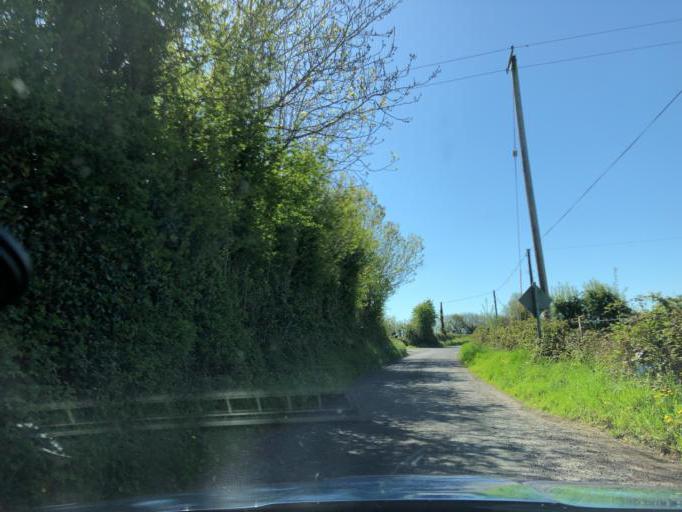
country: IE
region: Connaught
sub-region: County Galway
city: Portumna
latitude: 53.1279
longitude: -8.3309
